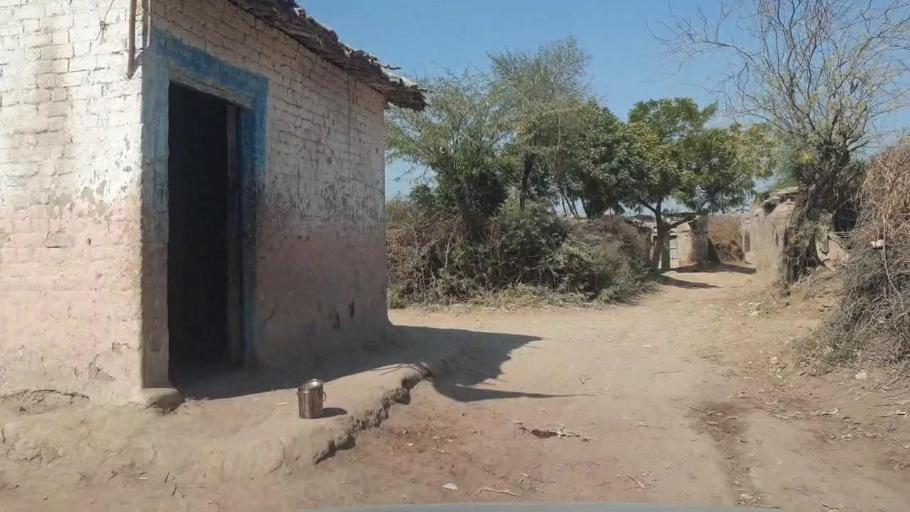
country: PK
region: Sindh
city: Chambar
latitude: 25.2309
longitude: 68.8496
